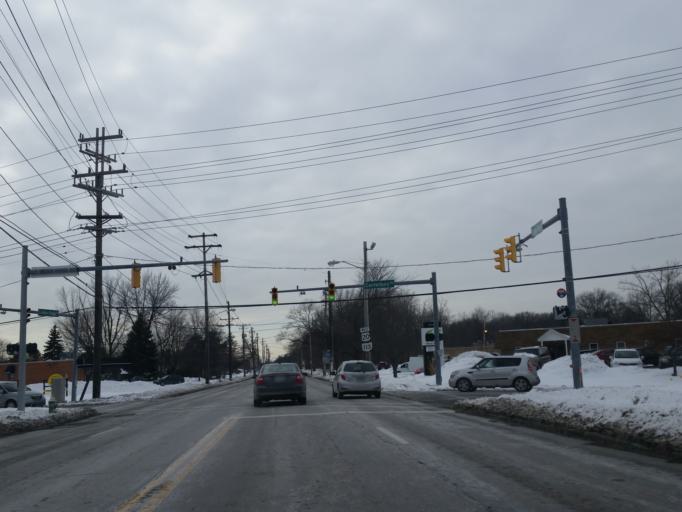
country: US
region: Ohio
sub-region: Cuyahoga County
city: Westlake
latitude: 41.4529
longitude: -81.9118
